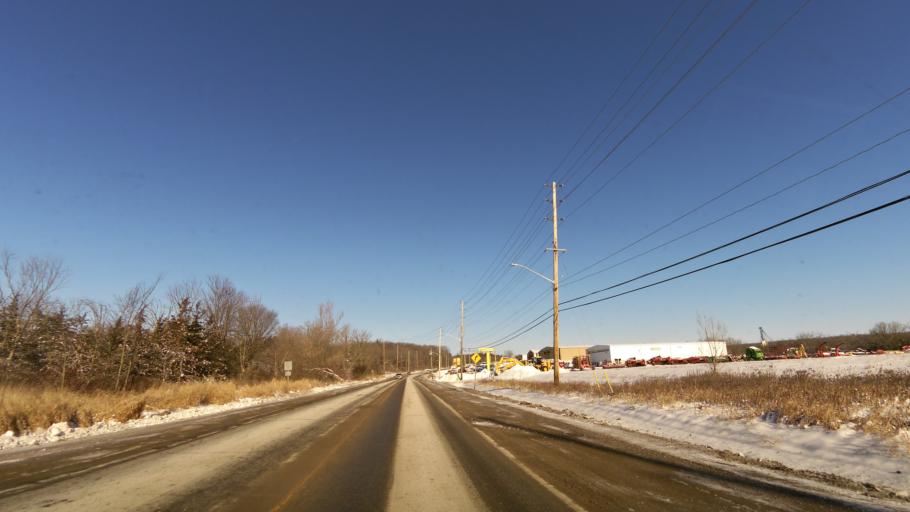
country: CA
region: Ontario
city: Quinte West
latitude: 44.2838
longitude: -77.8094
